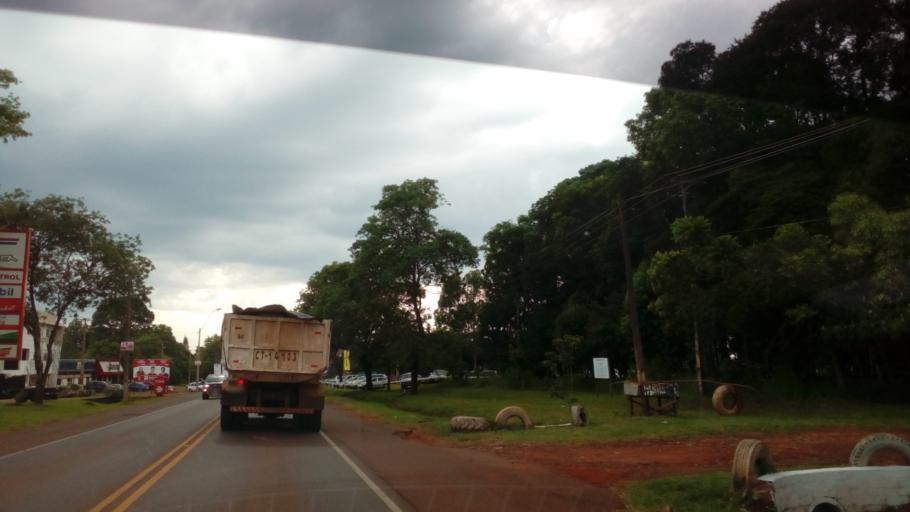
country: PY
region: Itapua
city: Obligado
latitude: -27.0721
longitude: -55.6340
